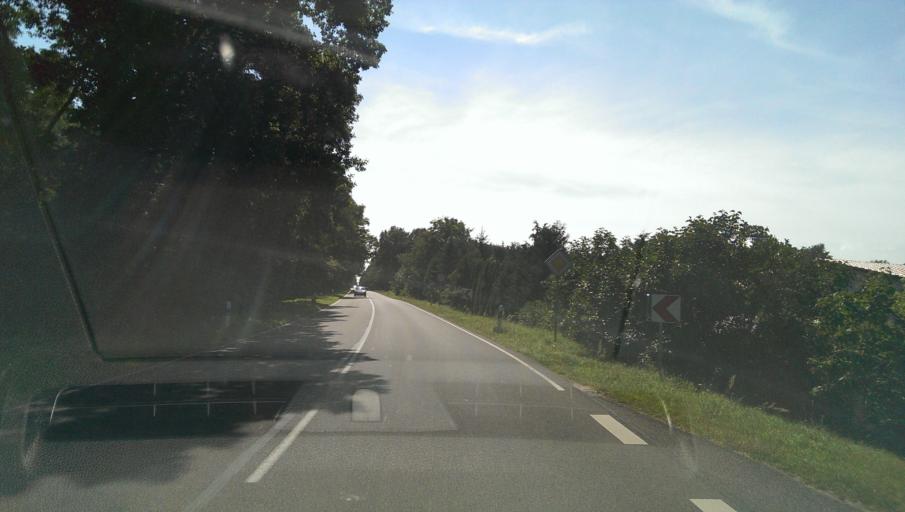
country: DE
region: Saxony-Anhalt
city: Kropstadt
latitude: 51.9578
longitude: 12.7392
